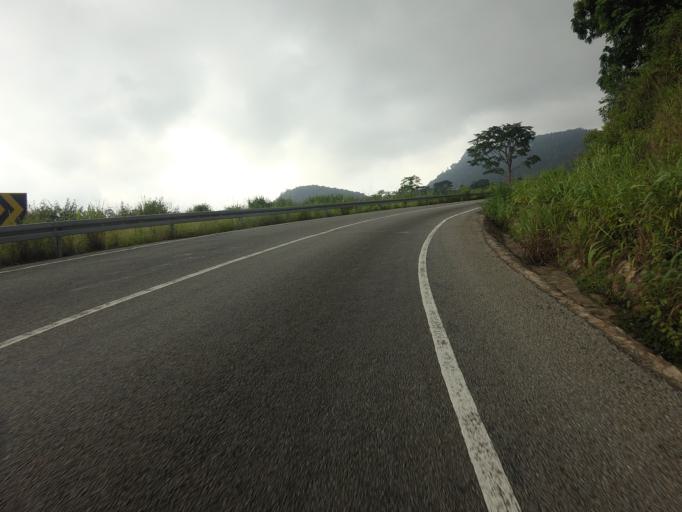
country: GH
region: Volta
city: Kpandu
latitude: 6.8165
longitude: 0.4224
